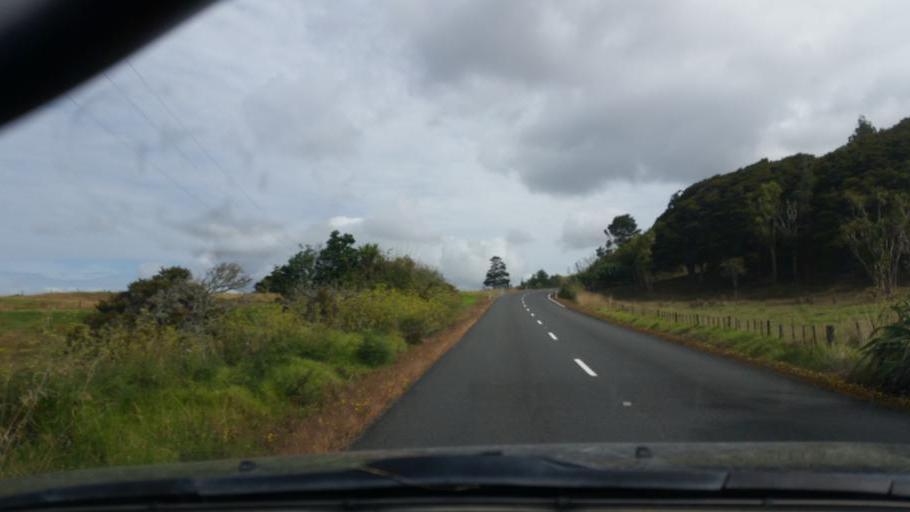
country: NZ
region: Northland
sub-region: Kaipara District
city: Dargaville
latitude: -35.9600
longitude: 173.9253
